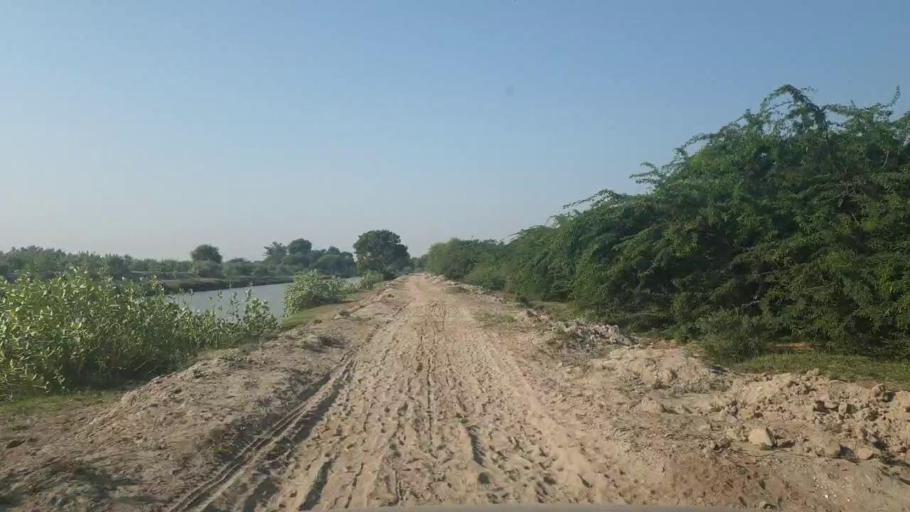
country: PK
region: Sindh
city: Tando Bago
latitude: 24.7204
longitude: 68.9176
